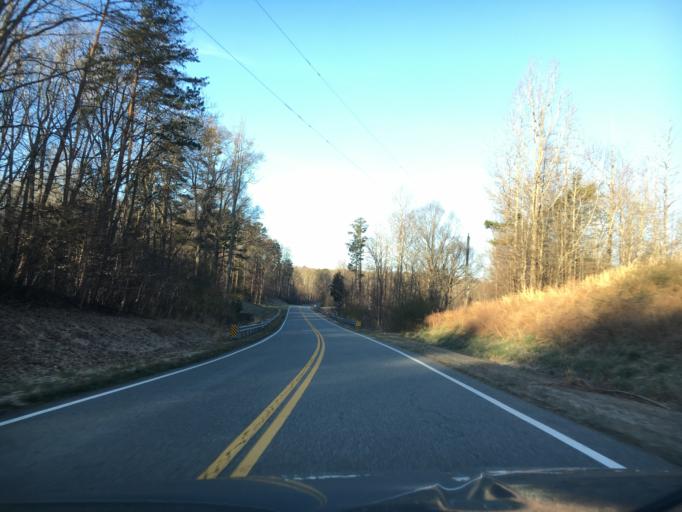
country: US
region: Virginia
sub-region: Halifax County
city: Halifax
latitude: 36.7613
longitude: -78.9014
